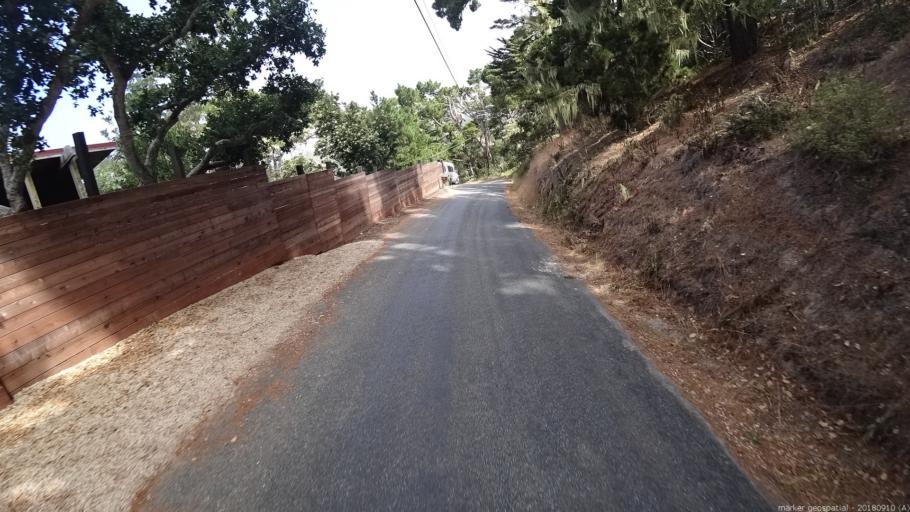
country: US
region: California
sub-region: Monterey County
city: Carmel-by-the-Sea
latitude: 36.5068
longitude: -121.9289
